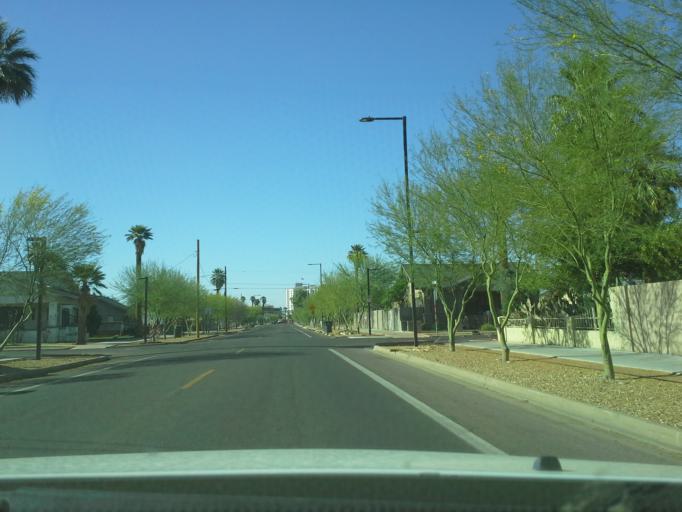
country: US
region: Arizona
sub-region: Maricopa County
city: Phoenix
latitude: 33.4564
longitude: -112.0589
